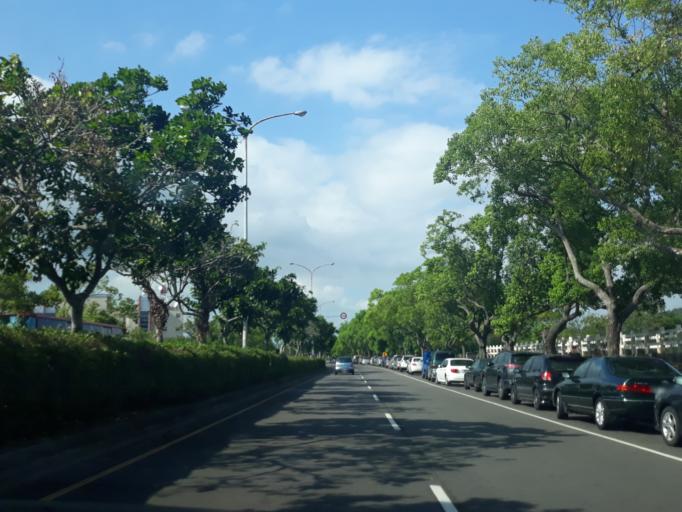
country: TW
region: Taiwan
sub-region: Miaoli
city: Miaoli
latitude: 24.5796
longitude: 120.8431
